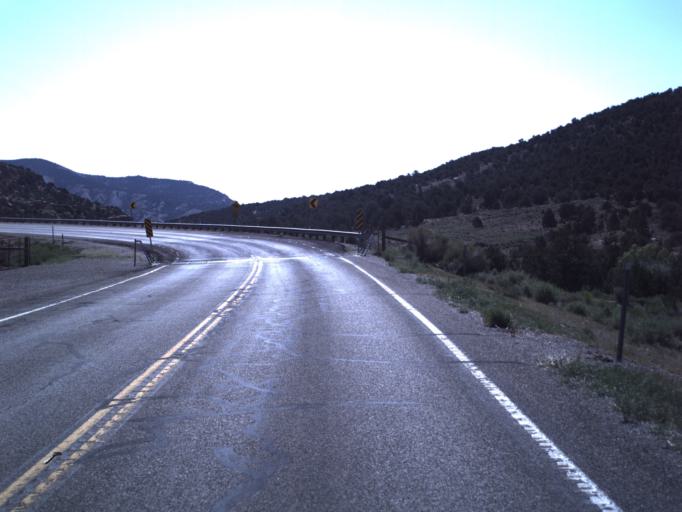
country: US
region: Utah
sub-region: Wayne County
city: Loa
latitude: 38.6720
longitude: -111.4075
